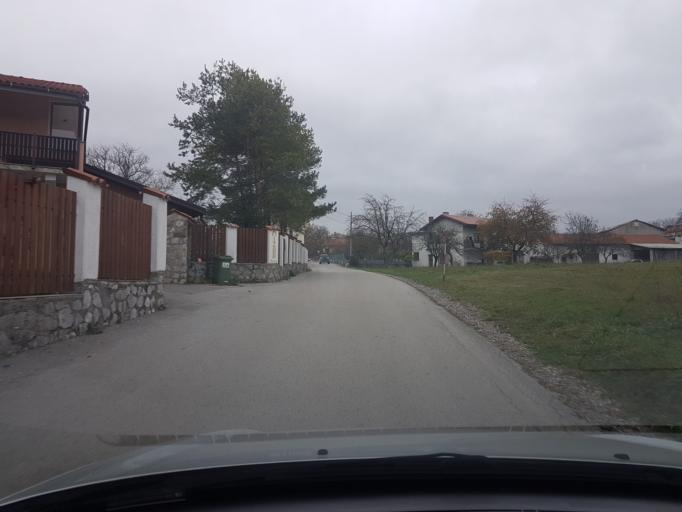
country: SI
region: Divaca
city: Divaca
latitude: 45.7307
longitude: 14.0096
